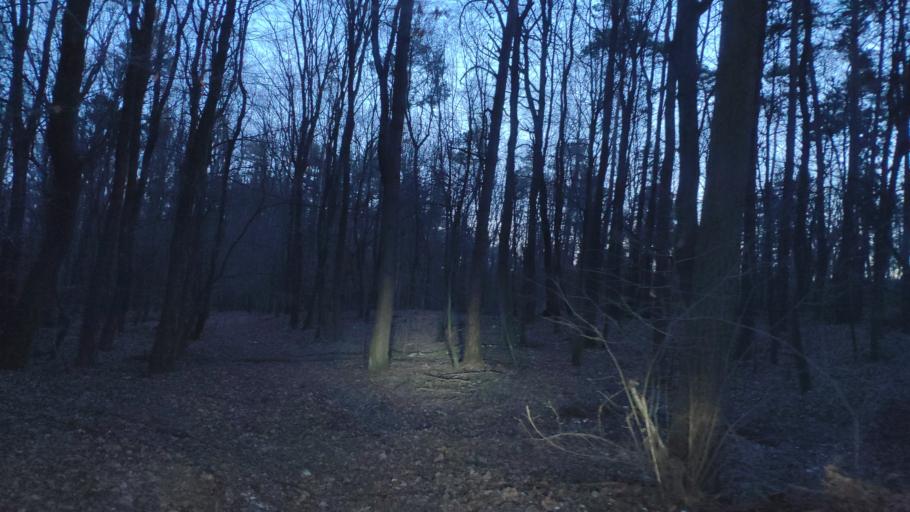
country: SK
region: Kosicky
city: Kosice
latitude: 48.8329
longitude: 21.2534
